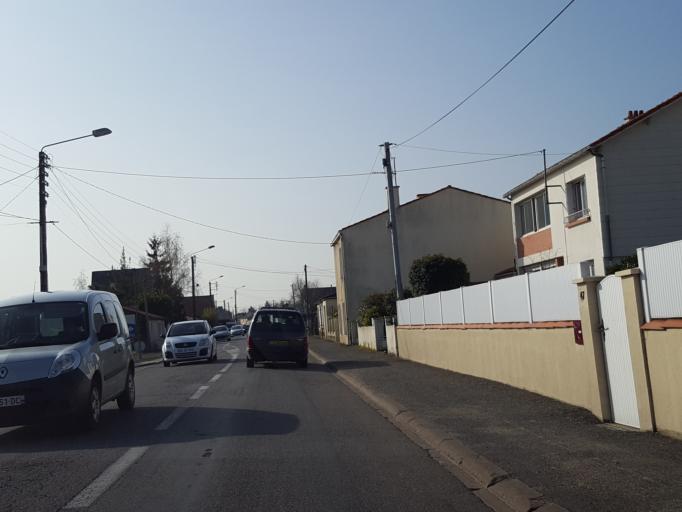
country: FR
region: Pays de la Loire
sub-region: Departement de la Loire-Atlantique
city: Geneston
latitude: 47.0596
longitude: -1.5149
